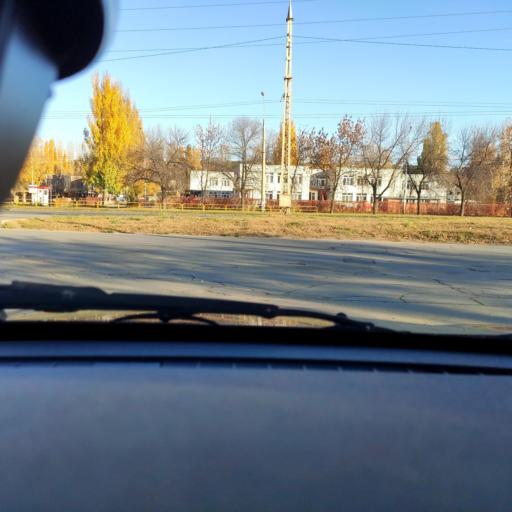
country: RU
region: Samara
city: Tol'yatti
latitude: 53.5085
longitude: 49.3019
